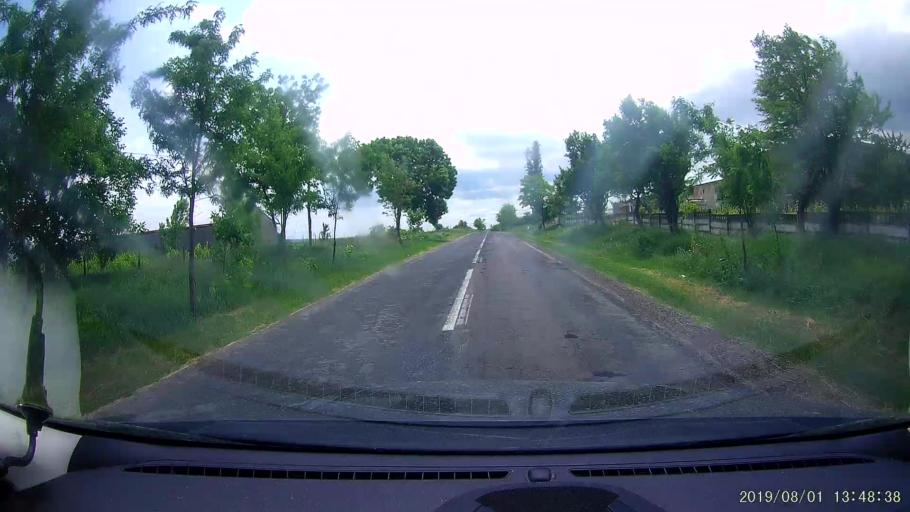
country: RO
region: Galati
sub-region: Comuna Oancea
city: Oancea
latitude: 45.9052
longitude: 28.1110
